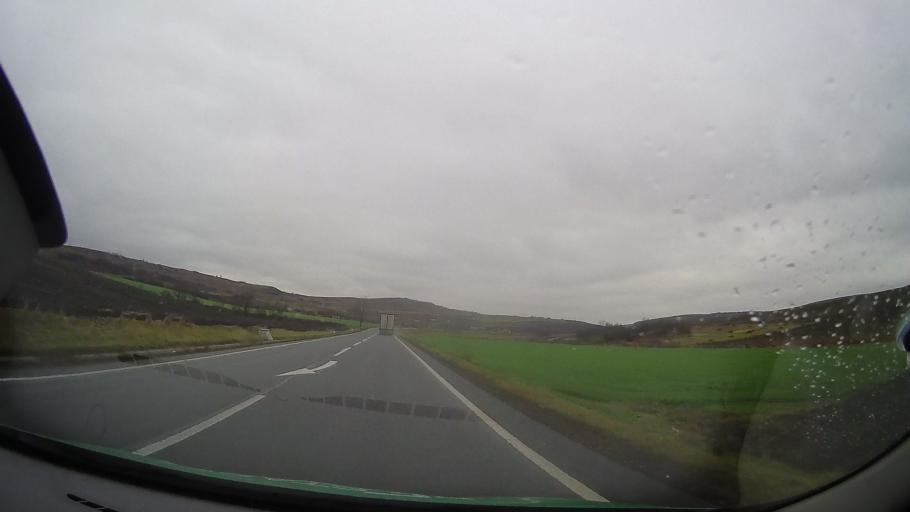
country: RO
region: Mures
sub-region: Comuna Lunca
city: Lunca
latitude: 46.8739
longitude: 24.5469
